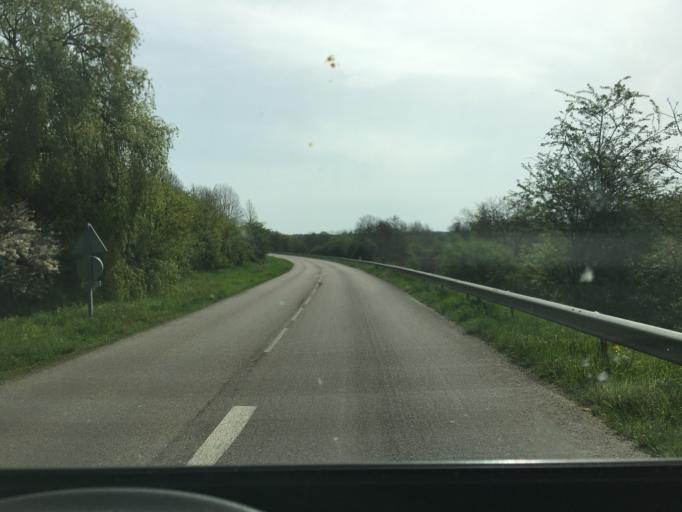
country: FR
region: Lorraine
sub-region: Departement de Meurthe-et-Moselle
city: Messein
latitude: 48.6120
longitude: 6.1261
